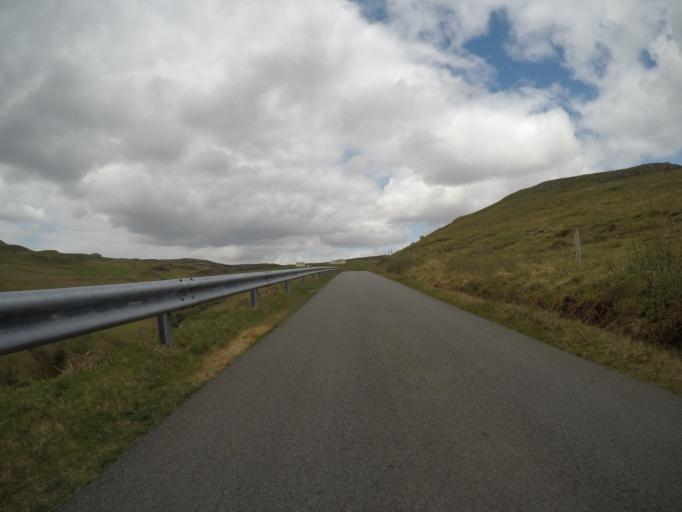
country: GB
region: Scotland
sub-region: Highland
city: Isle of Skye
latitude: 57.3631
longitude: -6.3973
